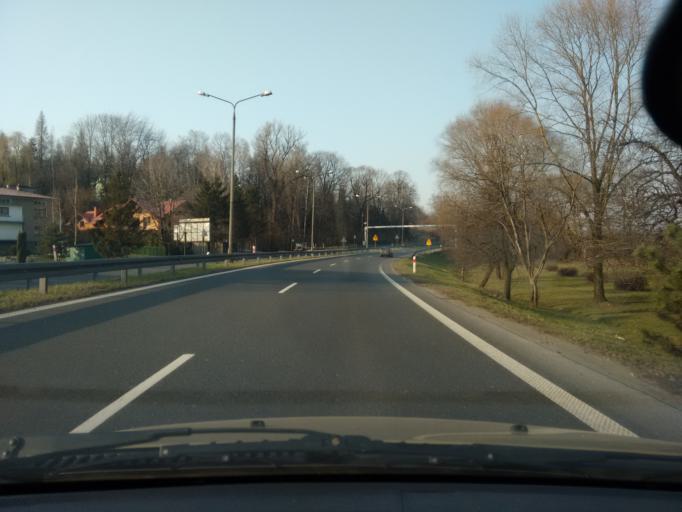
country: PL
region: Silesian Voivodeship
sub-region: Powiat cieszynski
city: Skoczow
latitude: 49.8080
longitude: 18.7898
